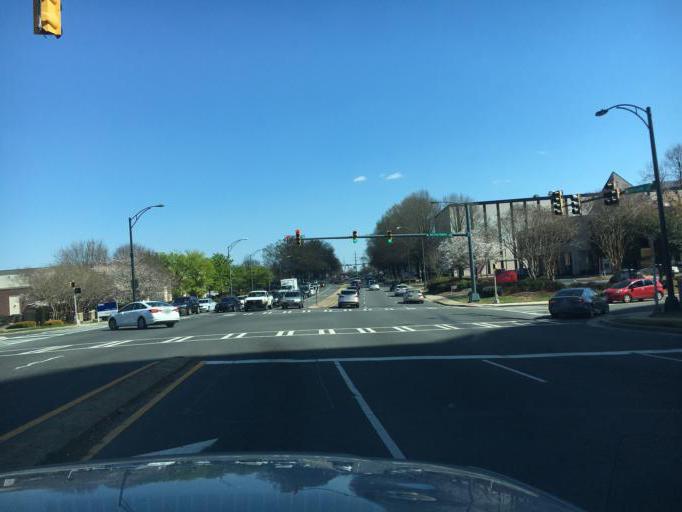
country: US
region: North Carolina
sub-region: Mecklenburg County
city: Charlotte
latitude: 35.1509
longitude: -80.8373
